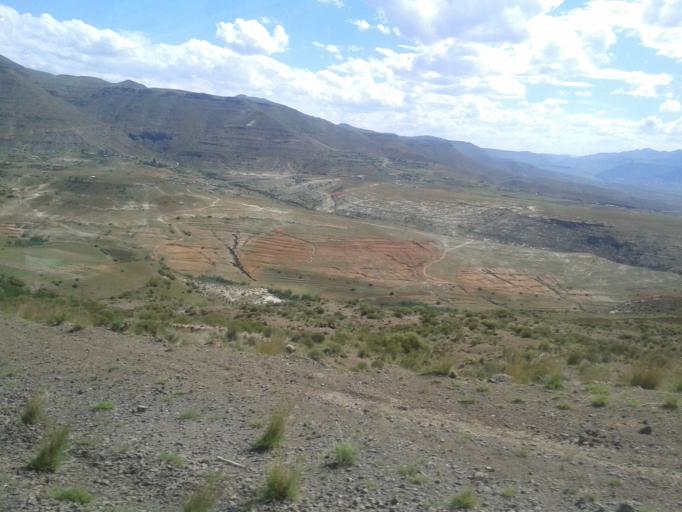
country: LS
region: Qacha's Nek
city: Qacha's Nek
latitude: -30.0454
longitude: 28.3085
